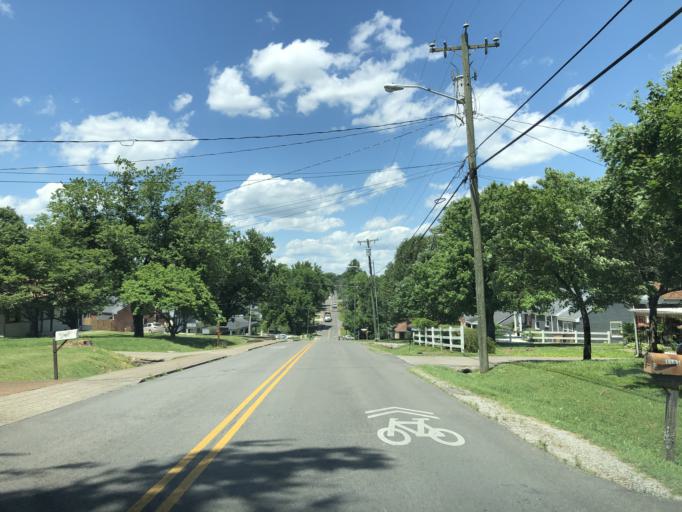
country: US
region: Tennessee
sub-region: Davidson County
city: Nashville
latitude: 36.1873
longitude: -86.7180
